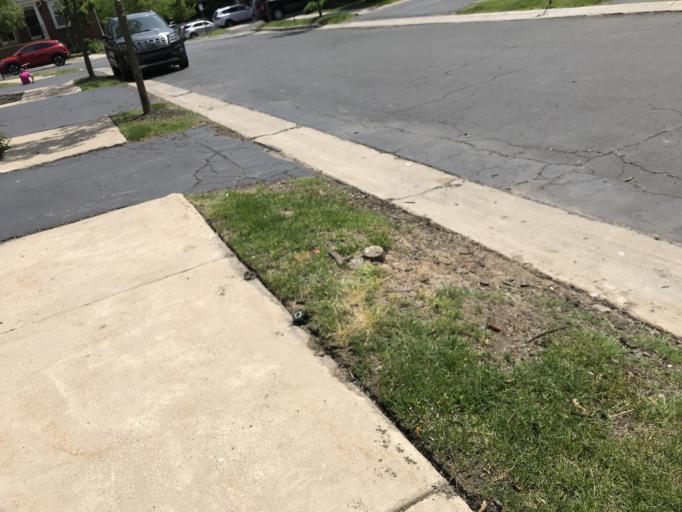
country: US
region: Michigan
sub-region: Oakland County
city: Novi
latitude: 42.4745
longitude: -83.4673
